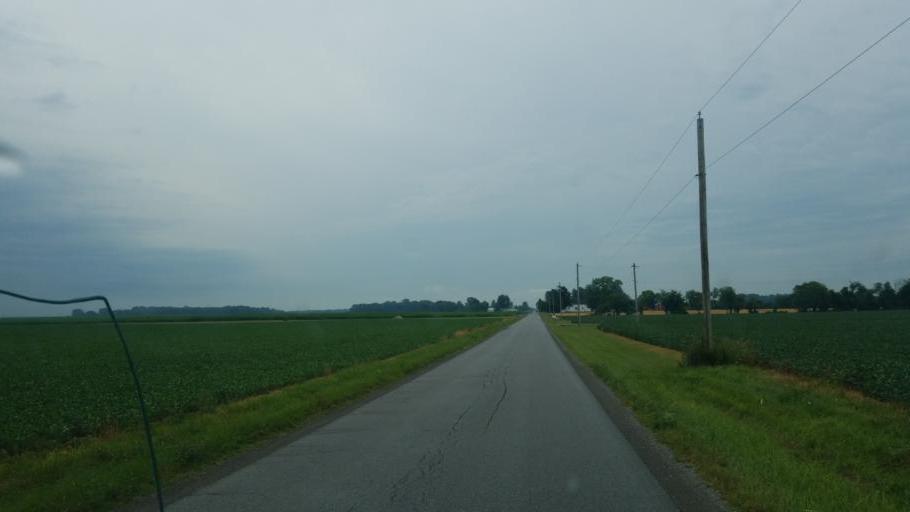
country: US
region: Ohio
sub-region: Williams County
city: Edgerton
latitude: 41.3893
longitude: -84.6699
